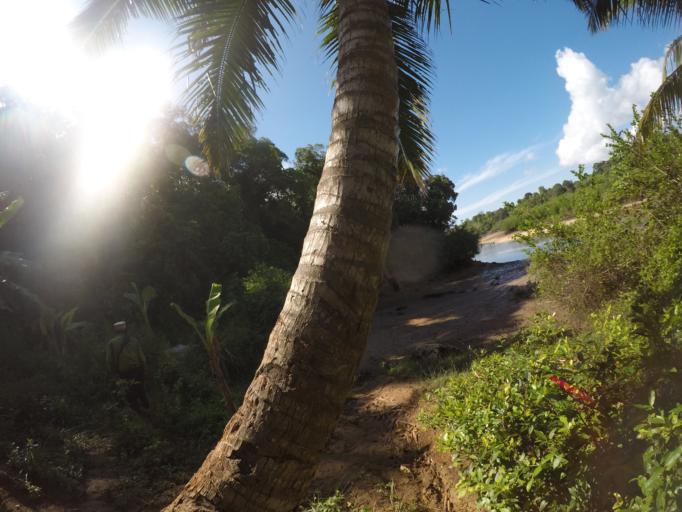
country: TZ
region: Pemba South
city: Mtambile
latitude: -5.3432
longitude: 39.6883
